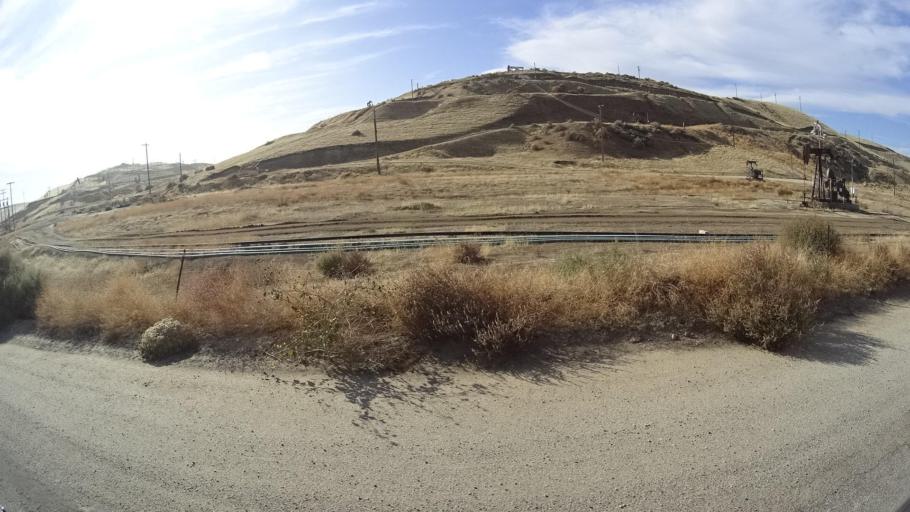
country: US
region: California
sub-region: Kern County
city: Oildale
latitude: 35.6118
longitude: -118.9723
